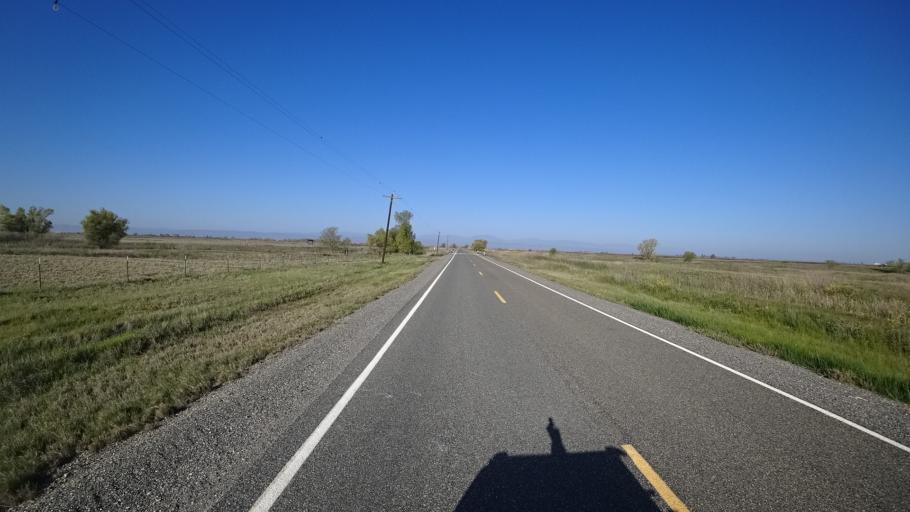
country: US
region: California
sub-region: Glenn County
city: Willows
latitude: 39.4074
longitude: -122.1431
